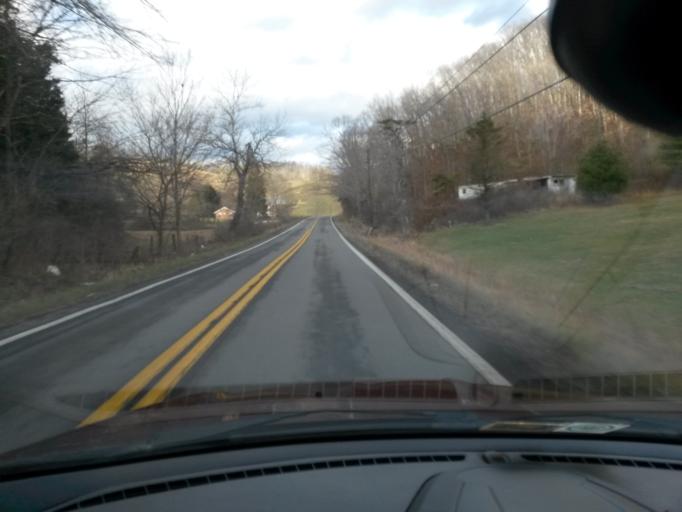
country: US
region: Virginia
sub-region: Giles County
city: Pembroke
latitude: 37.4642
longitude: -80.6604
